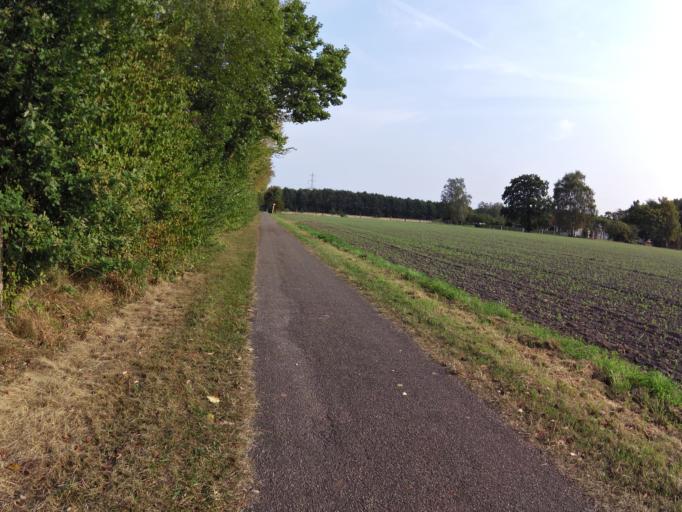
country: DE
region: North Rhine-Westphalia
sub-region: Regierungsbezirk Detmold
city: Petershagen
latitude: 52.3952
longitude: 8.9644
